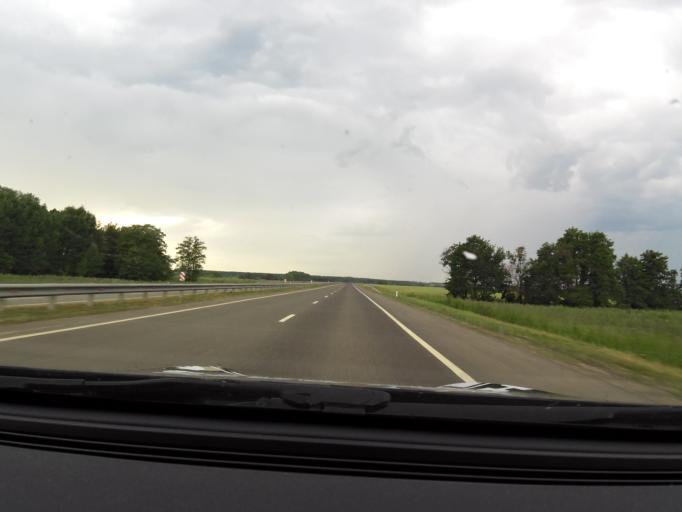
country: RU
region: Bashkortostan
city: Kushnarenkovo
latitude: 55.0607
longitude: 55.4061
